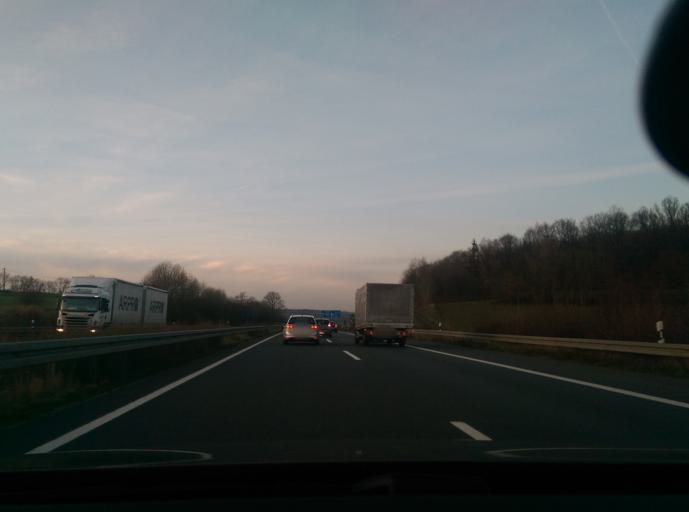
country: DE
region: Lower Saxony
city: Gemeinde Friedland
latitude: 51.4410
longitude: 9.8775
